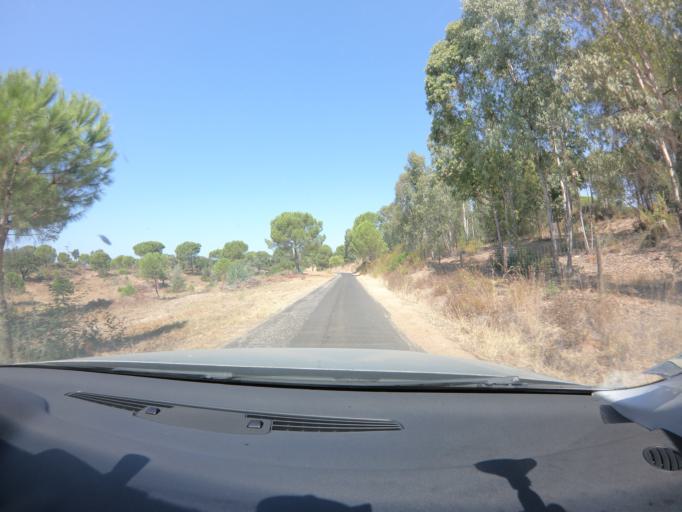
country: PT
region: Setubal
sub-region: Alcacer do Sal
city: Alcacer do Sal
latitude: 38.2519
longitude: -8.2978
